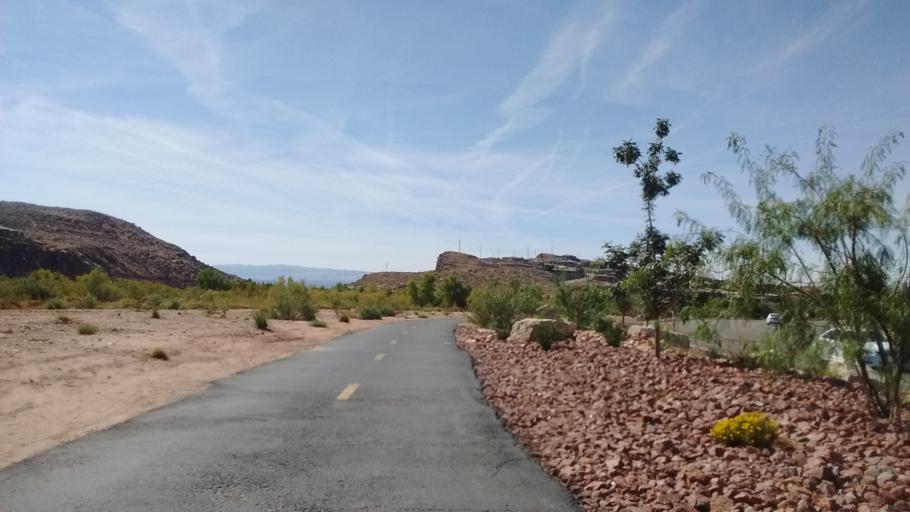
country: US
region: Utah
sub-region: Washington County
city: Saint George
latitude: 37.0760
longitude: -113.5790
